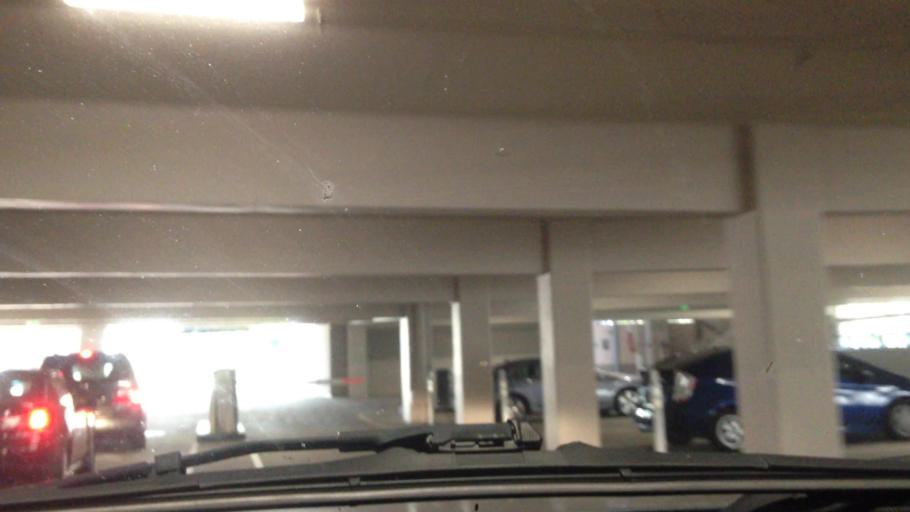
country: US
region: California
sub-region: Orange County
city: Irvine
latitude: 33.6784
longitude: -117.8541
